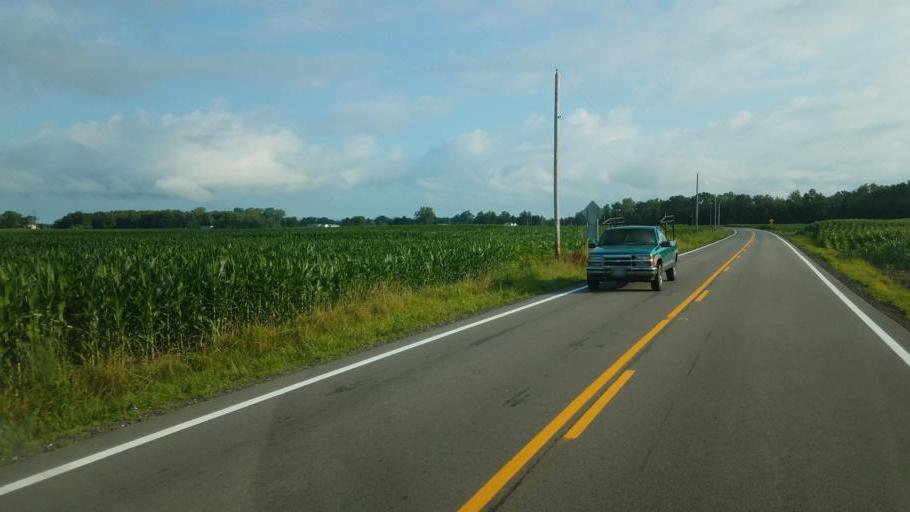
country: US
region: Ohio
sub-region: Richland County
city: Shelby
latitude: 40.8222
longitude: -82.6539
